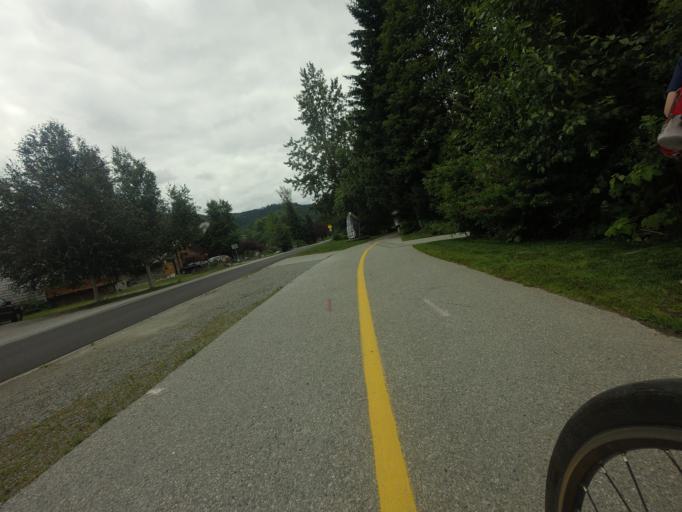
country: CA
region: British Columbia
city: Whistler
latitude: 50.0956
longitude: -122.9965
